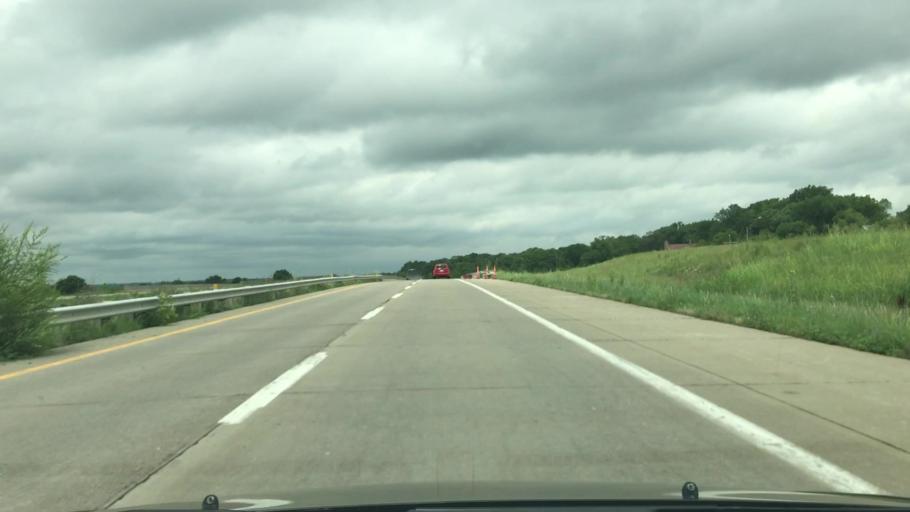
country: US
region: Missouri
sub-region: Jackson County
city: Grandview
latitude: 38.8620
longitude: -94.5838
